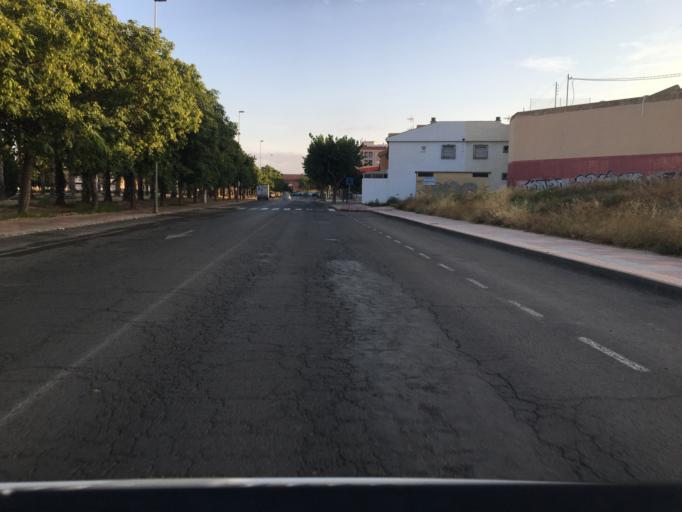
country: ES
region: Murcia
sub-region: Murcia
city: Cartagena
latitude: 37.6201
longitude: -0.9903
